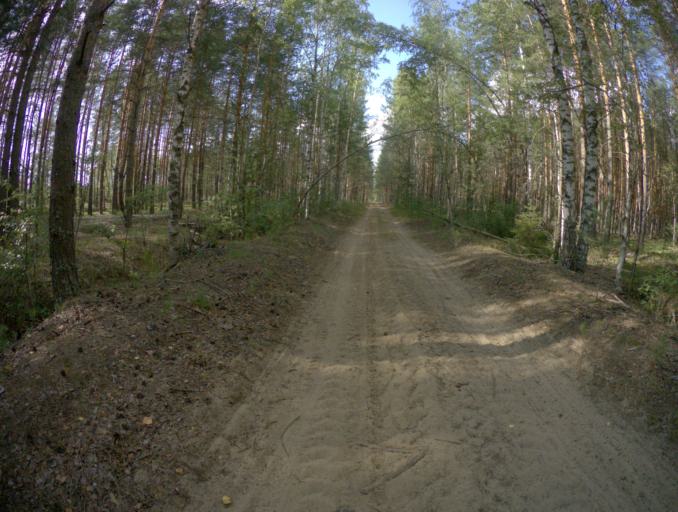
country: RU
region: Vladimir
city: Sobinka
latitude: 55.9274
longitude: 40.0648
